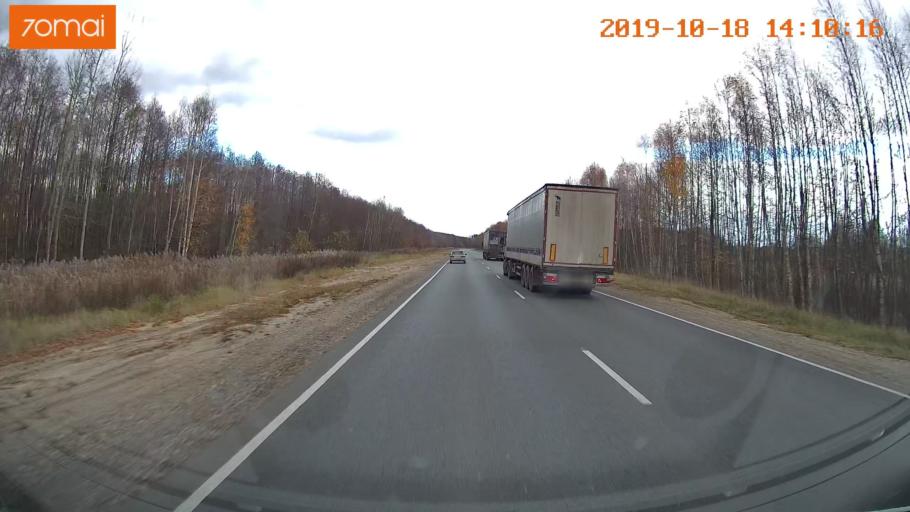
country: RU
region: Rjazan
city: Spas-Klepiki
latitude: 55.1427
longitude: 40.2021
